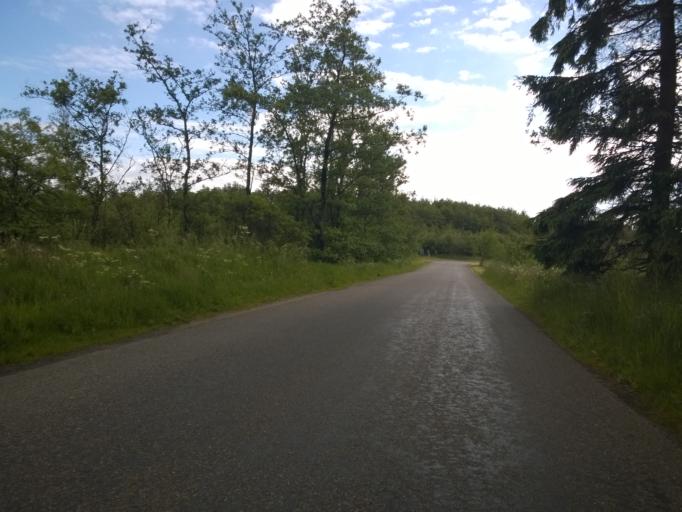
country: DK
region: Central Jutland
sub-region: Holstebro Kommune
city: Vinderup
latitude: 56.5114
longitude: 8.8245
